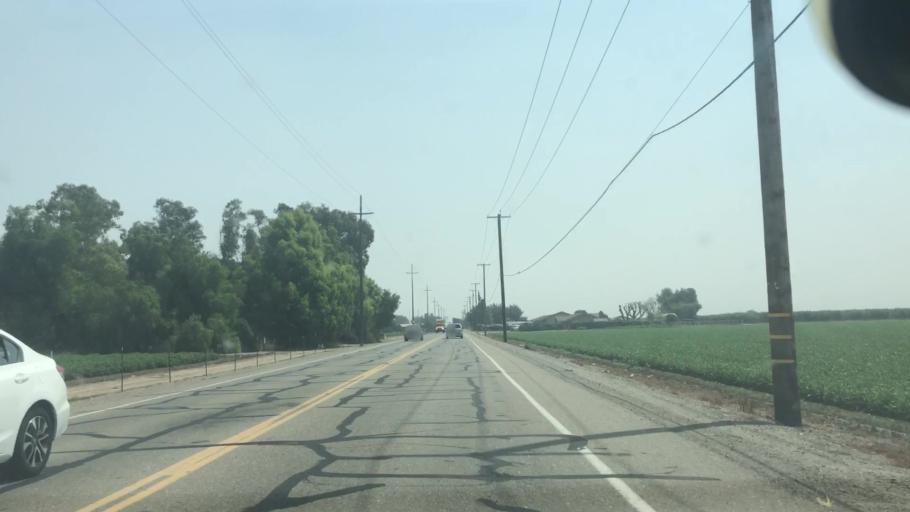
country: US
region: California
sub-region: San Joaquin County
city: Tracy
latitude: 37.7319
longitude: -121.3983
